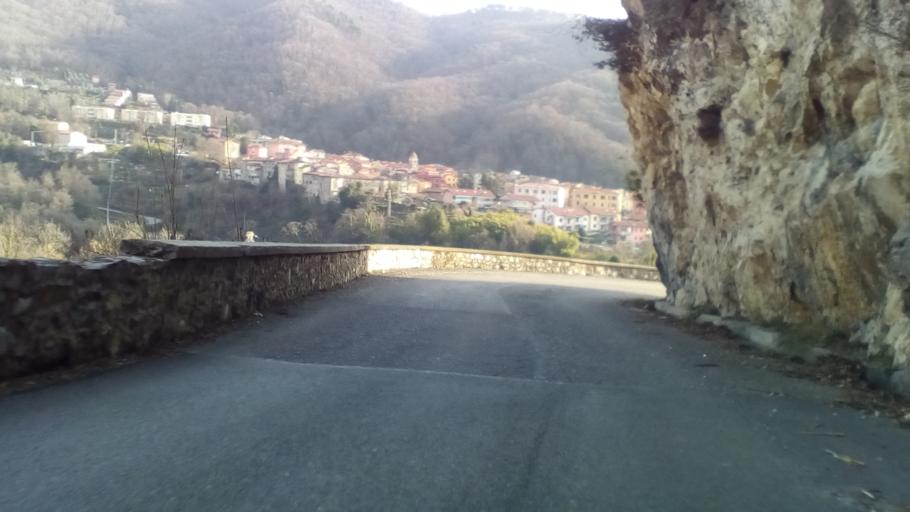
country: IT
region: Tuscany
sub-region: Provincia di Massa-Carrara
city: Massa
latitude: 44.0836
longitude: 10.1232
